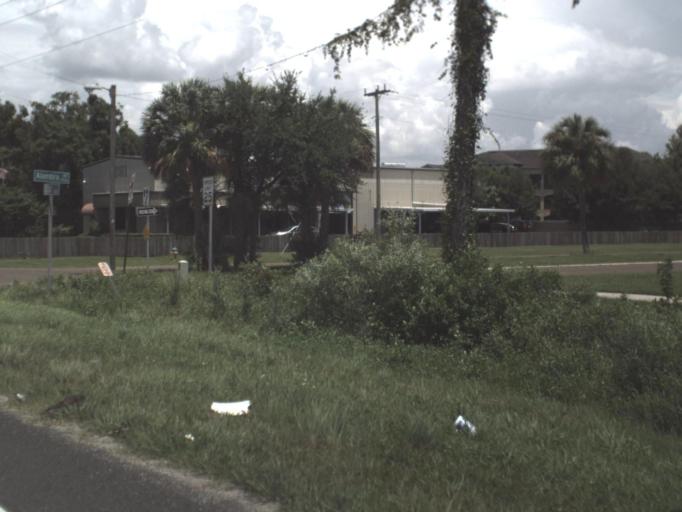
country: US
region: Florida
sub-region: Hillsborough County
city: Progress Village
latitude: 27.9242
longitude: -82.3500
